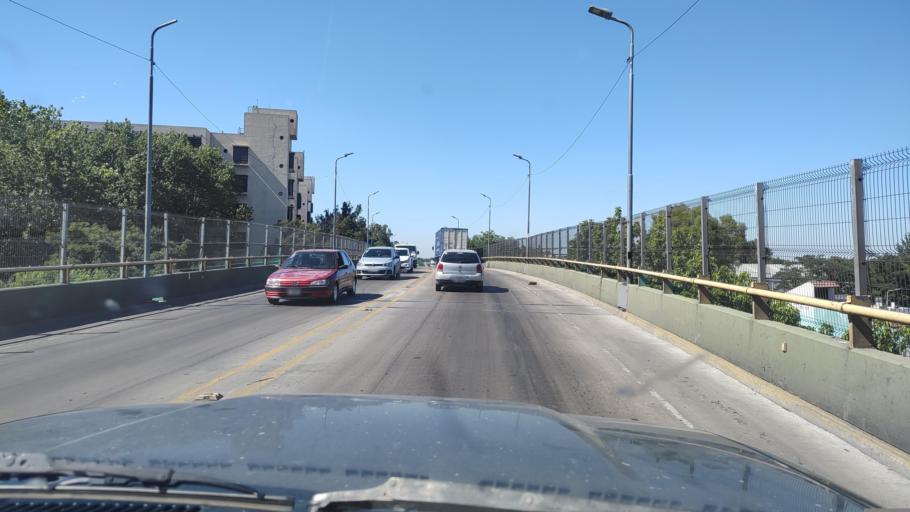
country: AR
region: Buenos Aires
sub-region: Partido de Moron
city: Moron
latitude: -34.6483
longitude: -58.6287
